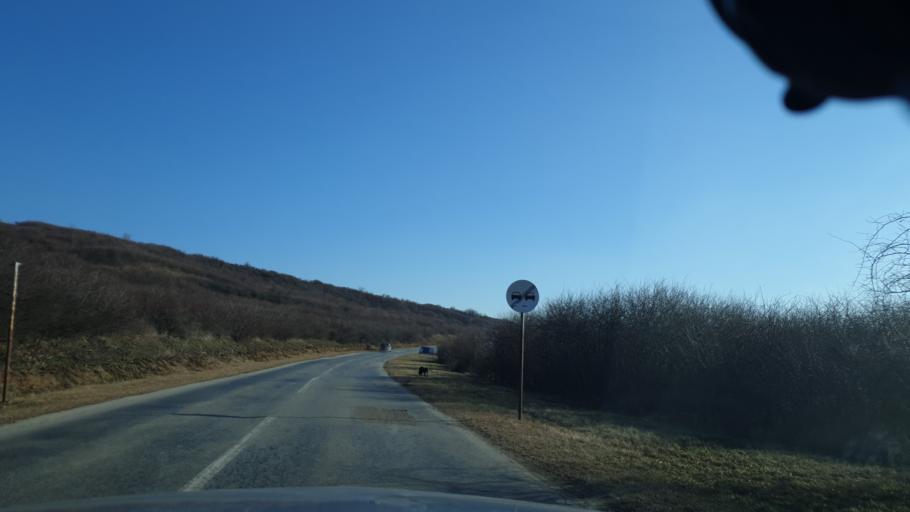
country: RS
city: Vrdnik
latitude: 45.1028
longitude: 19.8024
